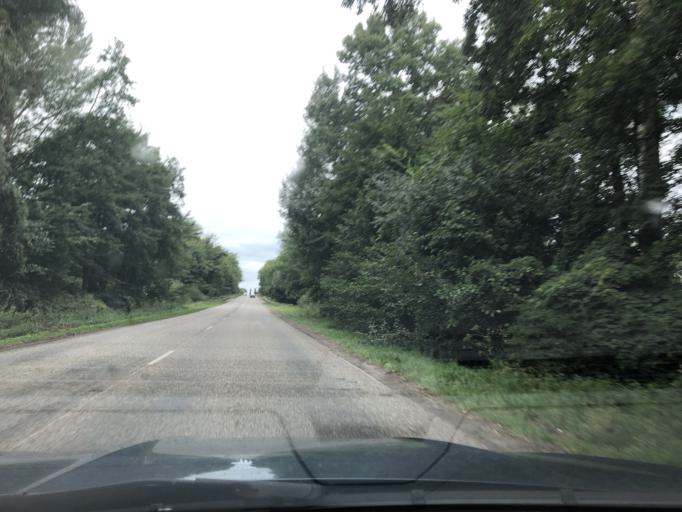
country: DE
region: Rheinland-Pfalz
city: Scheibenhardt
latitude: 48.9719
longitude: 8.1654
